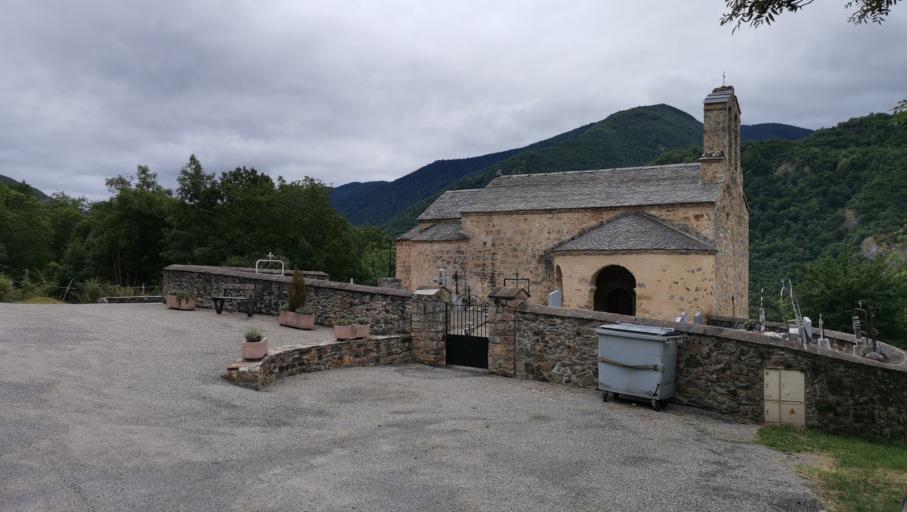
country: FR
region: Midi-Pyrenees
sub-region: Departement de l'Ariege
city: Ax-les-Thermes
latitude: 42.7704
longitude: 1.7555
